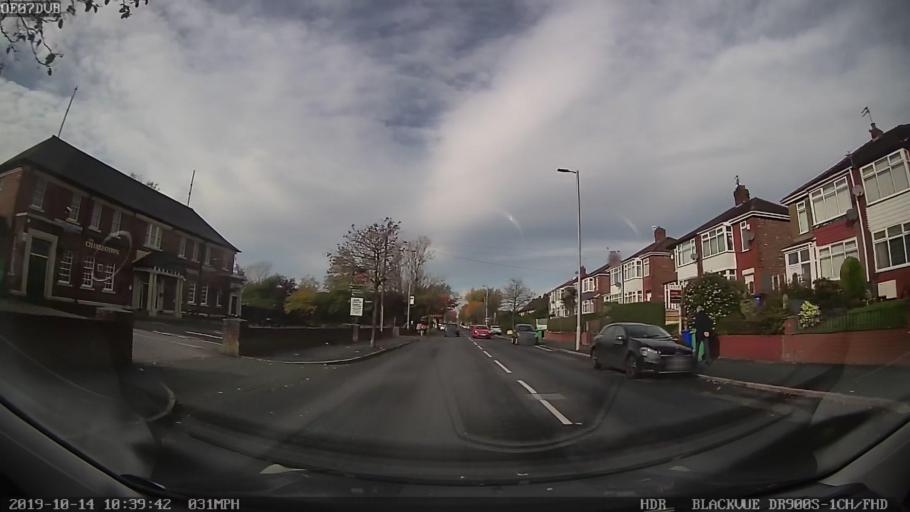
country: GB
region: England
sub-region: Manchester
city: Blackley
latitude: 53.5229
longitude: -2.1875
